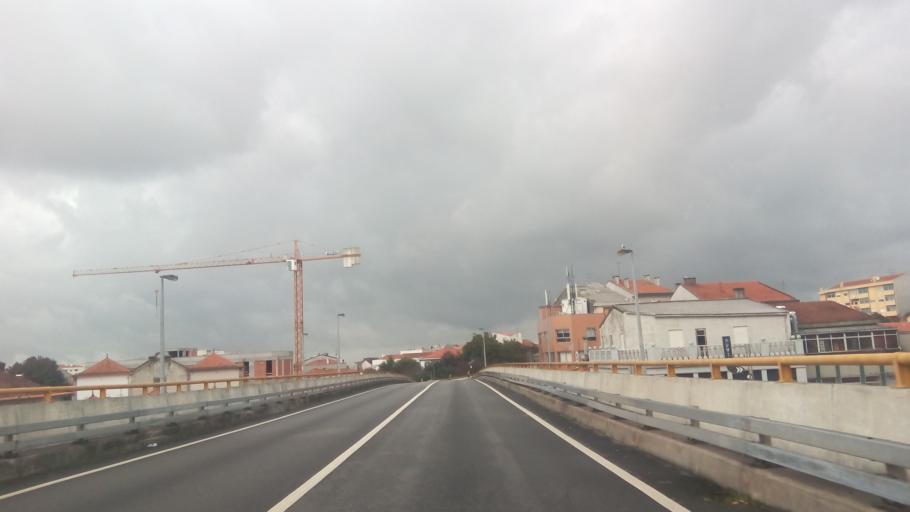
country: PT
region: Porto
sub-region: Maia
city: Pedroucos
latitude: 41.1807
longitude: -8.5823
